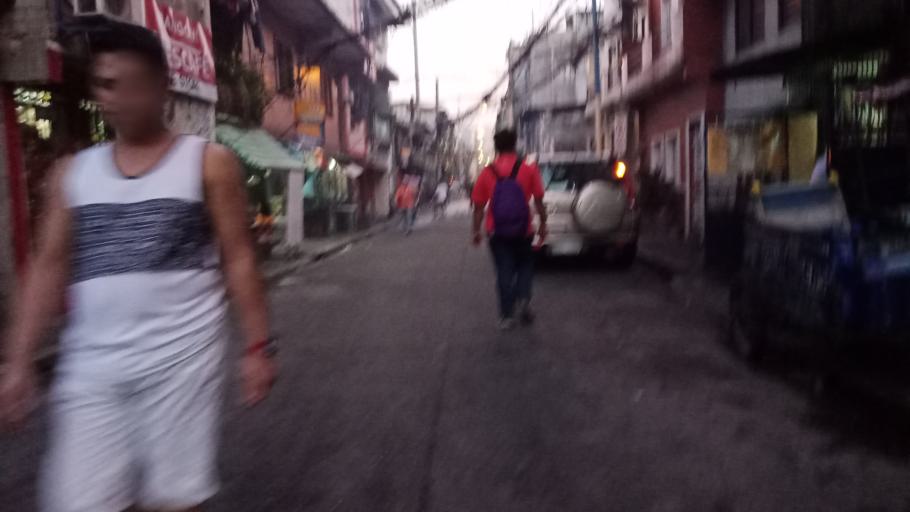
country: PH
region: Metro Manila
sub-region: San Juan
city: San Juan
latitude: 14.5907
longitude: 121.0300
